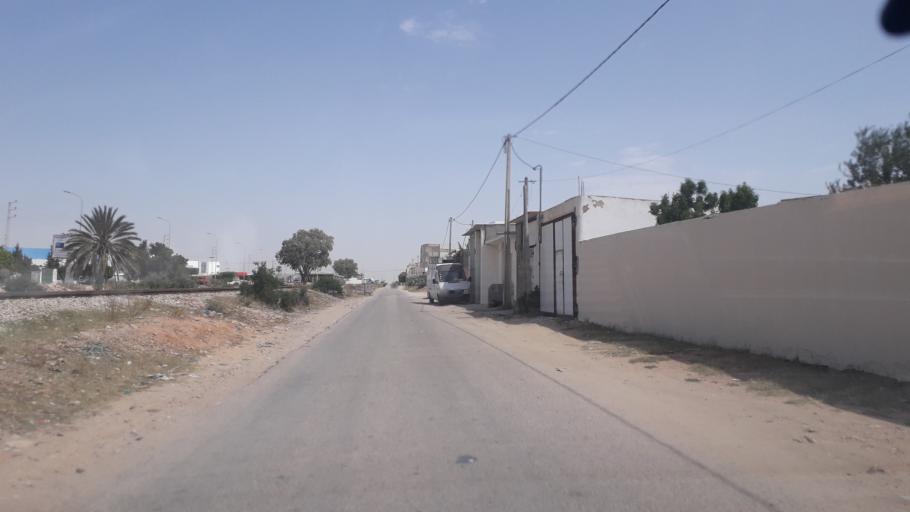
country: TN
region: Safaqis
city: Al Qarmadah
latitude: 34.8310
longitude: 10.7650
